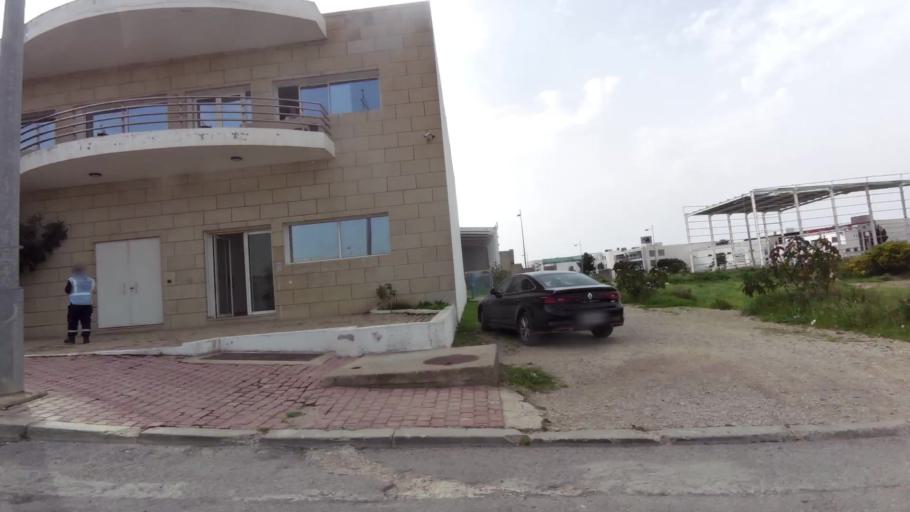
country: MA
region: Tanger-Tetouan
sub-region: Tanger-Assilah
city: Boukhalef
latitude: 35.7138
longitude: -5.9063
